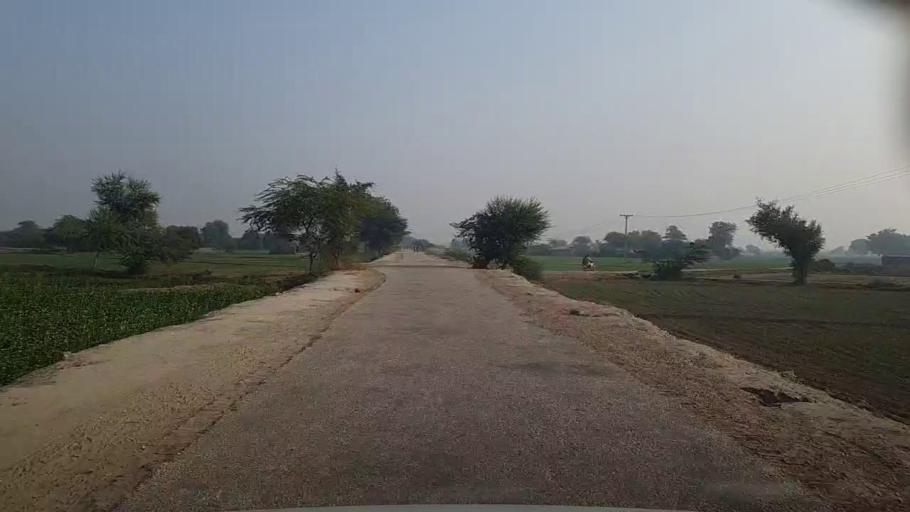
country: PK
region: Sindh
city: Kandiari
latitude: 27.0486
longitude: 68.4691
